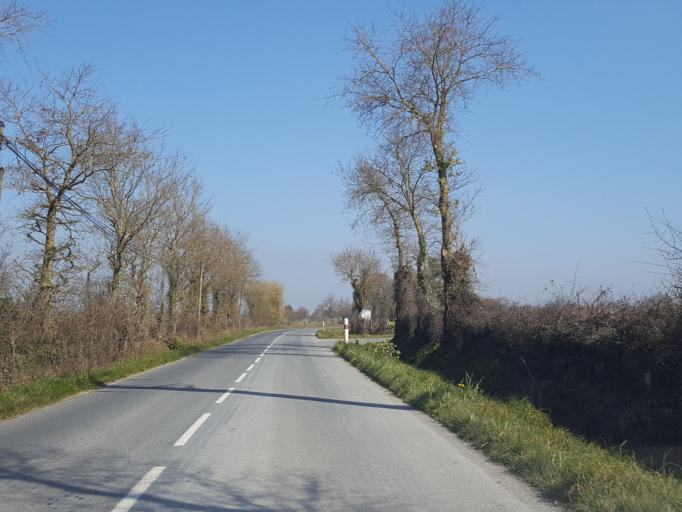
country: FR
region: Pays de la Loire
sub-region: Departement de la Vendee
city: La Chaize-le-Vicomte
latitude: 46.6629
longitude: -1.2966
